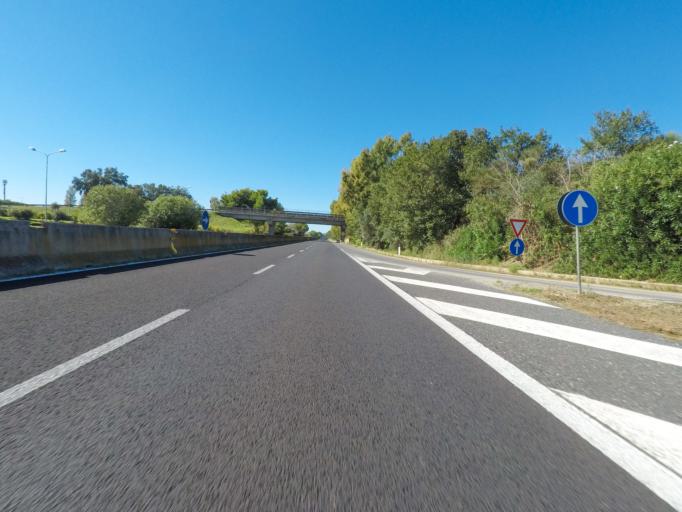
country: IT
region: Latium
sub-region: Provincia di Viterbo
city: Pescia Romana
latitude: 42.4024
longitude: 11.4997
